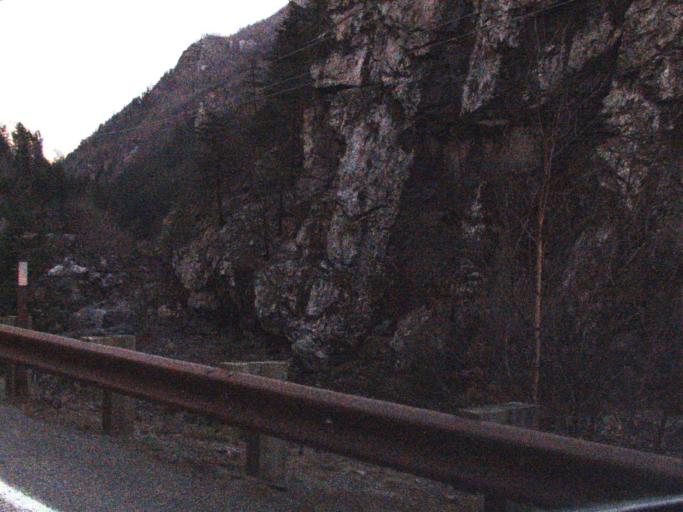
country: US
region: Washington
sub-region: Snohomish County
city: Darrington
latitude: 48.6866
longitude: -121.2381
